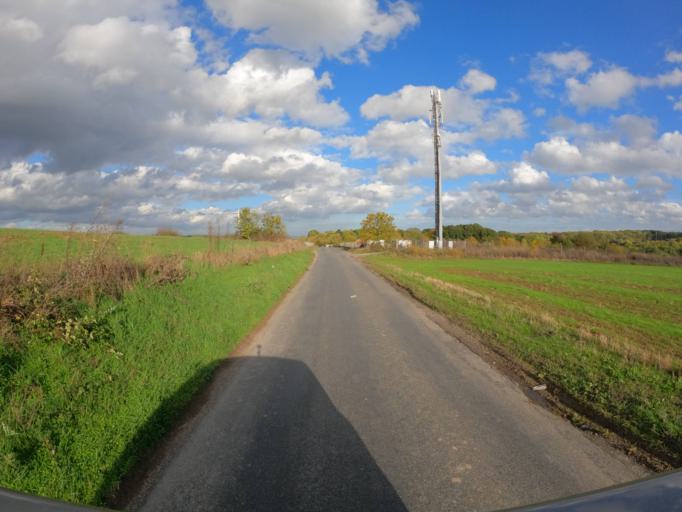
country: FR
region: Ile-de-France
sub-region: Departement de Seine-et-Marne
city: Chalifert
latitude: 48.8891
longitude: 2.7821
